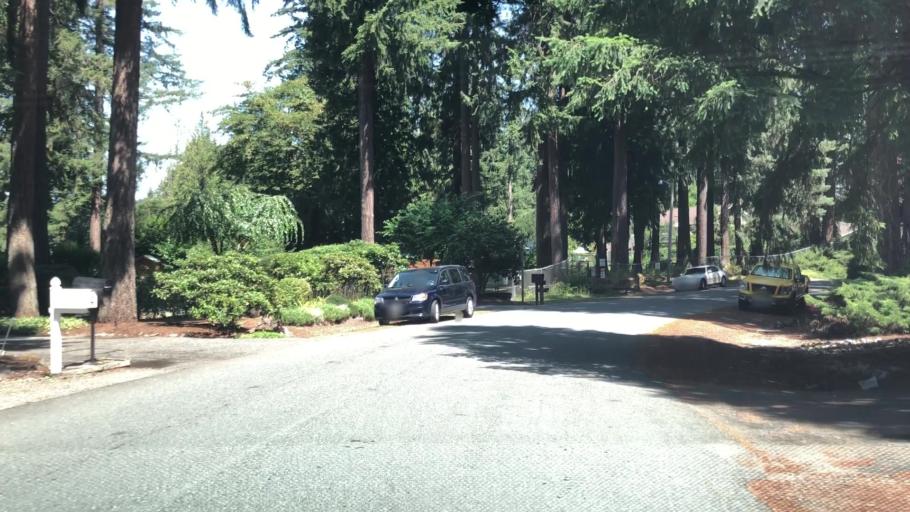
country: US
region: Washington
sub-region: King County
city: Cottage Lake
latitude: 47.7502
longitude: -122.0867
